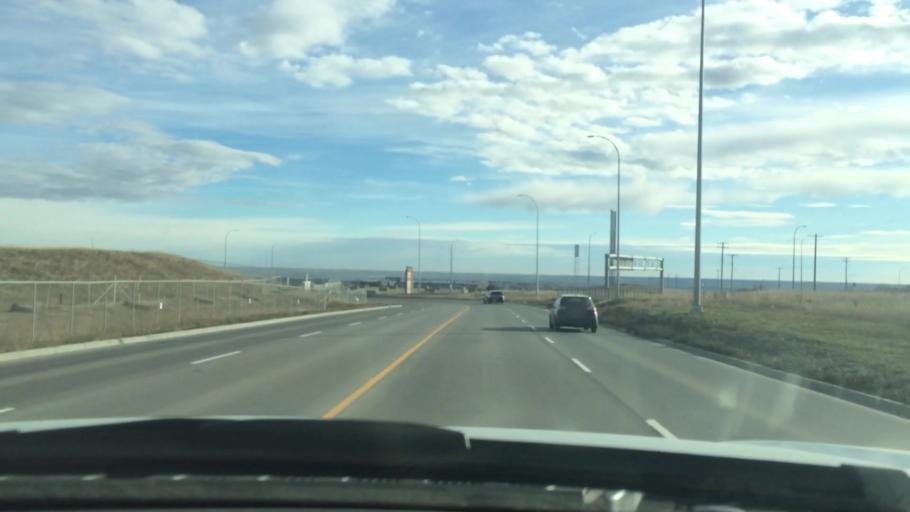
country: CA
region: Alberta
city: Calgary
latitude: 51.1543
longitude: -114.1672
